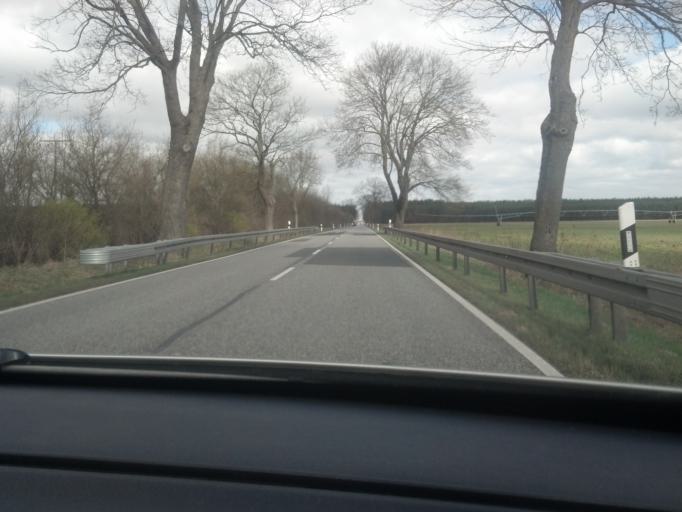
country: DE
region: Mecklenburg-Vorpommern
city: Plau am See
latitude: 53.3554
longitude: 12.2469
